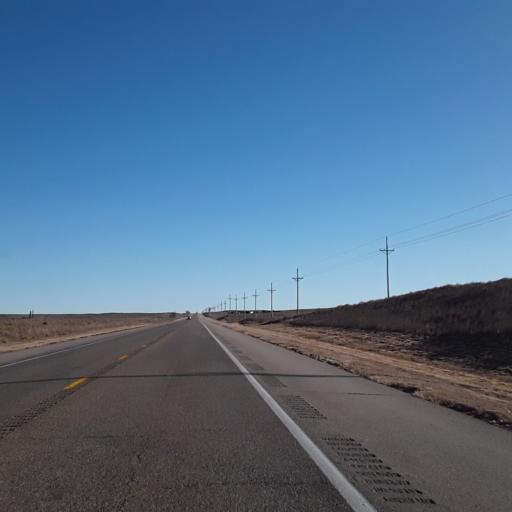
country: US
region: Kansas
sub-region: Meade County
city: Meade
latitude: 37.3907
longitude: -100.1603
